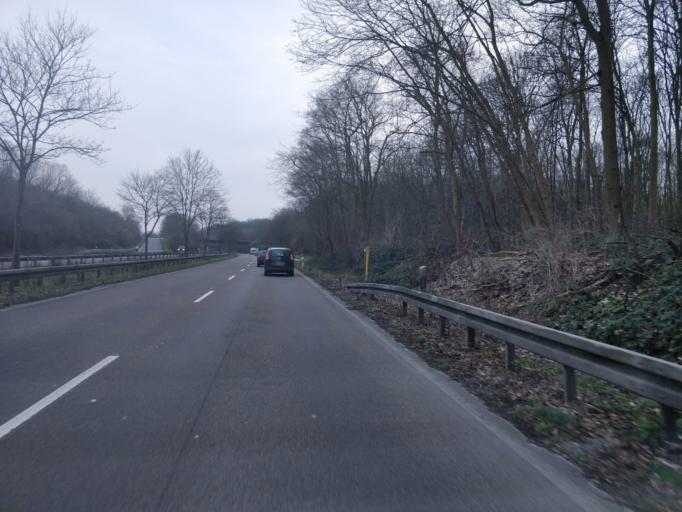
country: DE
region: North Rhine-Westphalia
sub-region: Regierungsbezirk Koln
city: Mengenich
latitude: 50.9544
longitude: 6.8699
